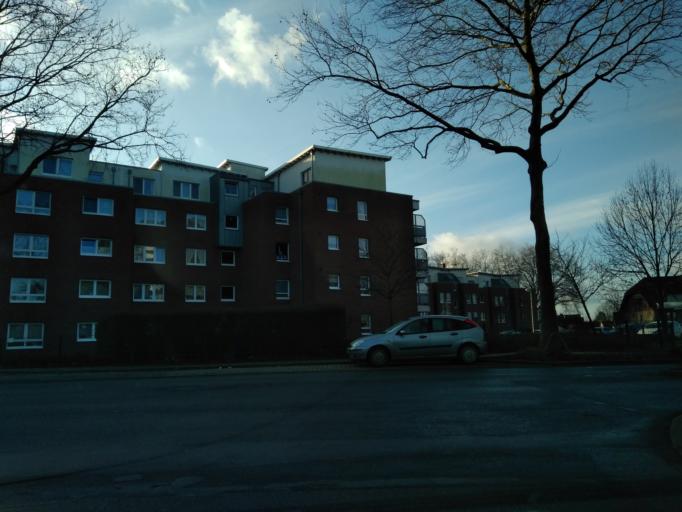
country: DE
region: North Rhine-Westphalia
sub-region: Regierungsbezirk Munster
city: Gladbeck
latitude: 51.5803
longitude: 6.9631
